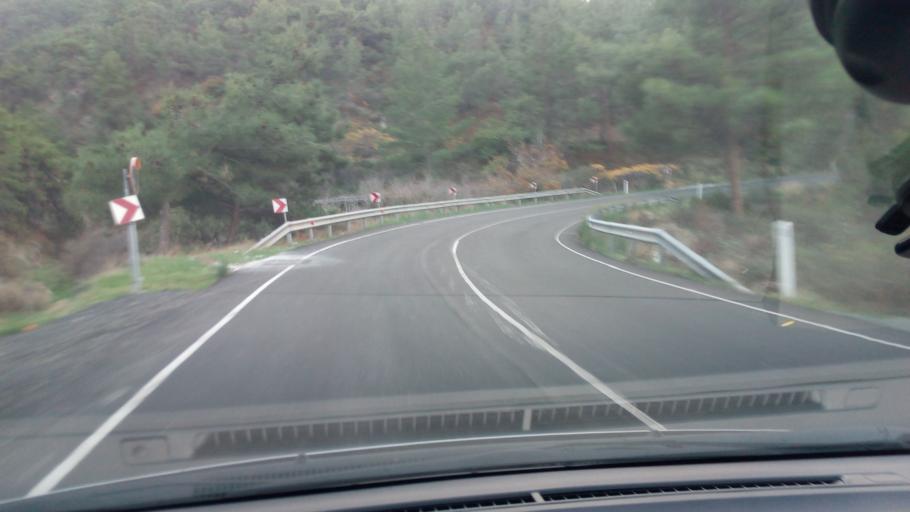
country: CY
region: Pafos
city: Polis
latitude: 35.1459
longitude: 32.5328
